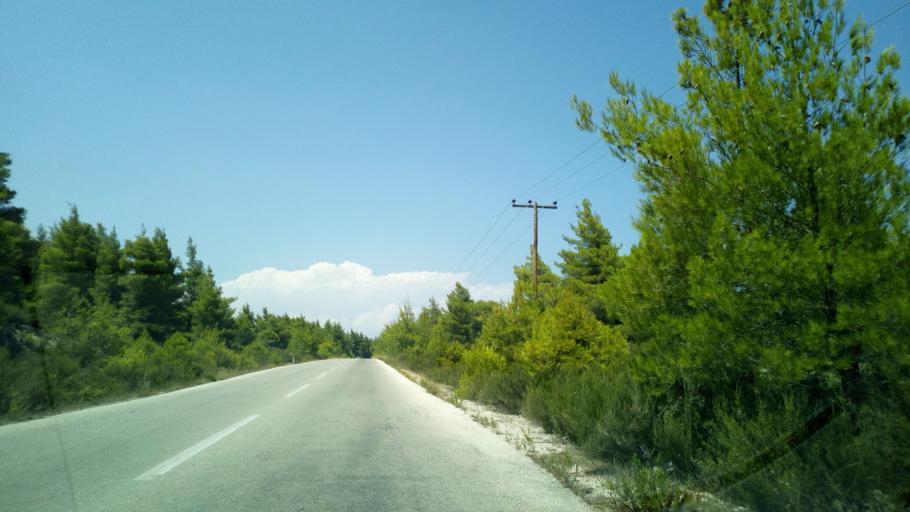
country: GR
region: Central Macedonia
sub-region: Nomos Chalkidikis
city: Sarti
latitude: 40.1325
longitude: 23.9262
